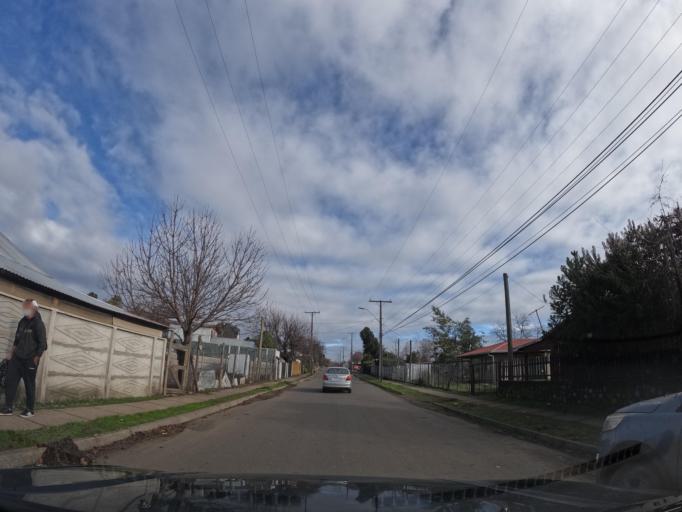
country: CL
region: Biobio
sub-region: Provincia de Nuble
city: Coihueco
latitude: -36.7002
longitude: -71.8983
